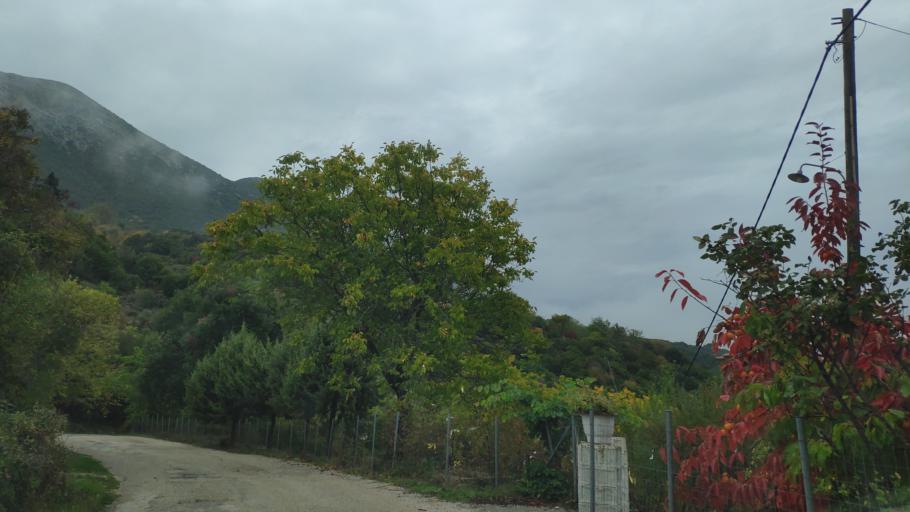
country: GR
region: Epirus
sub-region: Nomos Thesprotias
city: Paramythia
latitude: 39.4634
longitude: 20.6728
